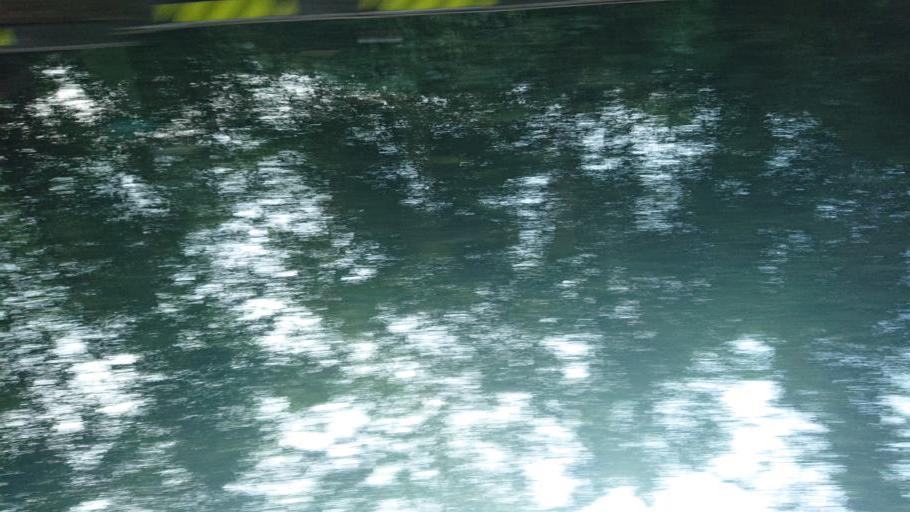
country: TW
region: Taiwan
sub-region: Chiayi
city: Jiayi Shi
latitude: 23.4626
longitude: 120.7212
